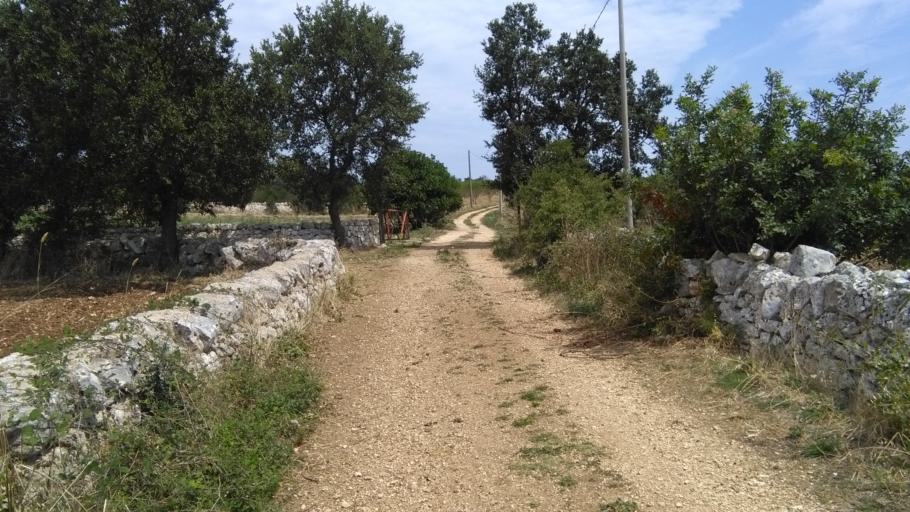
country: IT
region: Apulia
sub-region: Provincia di Bari
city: Gioia del Colle
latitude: 40.8276
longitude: 16.9855
